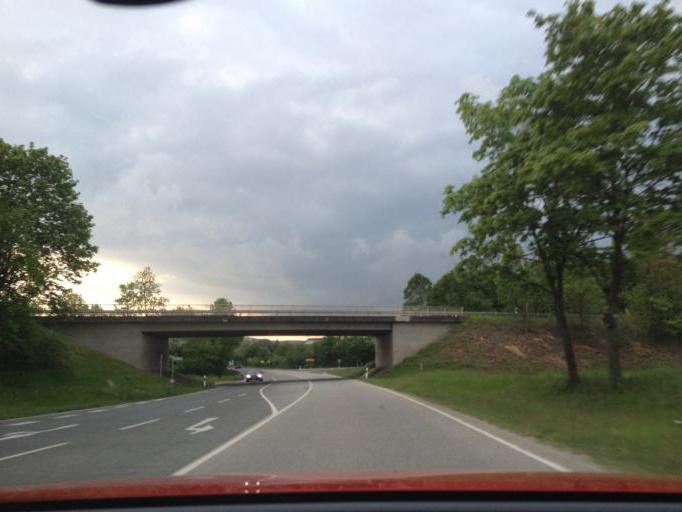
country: DE
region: Bavaria
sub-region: Upper Palatinate
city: Hahnbach
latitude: 49.5364
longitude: 11.8137
